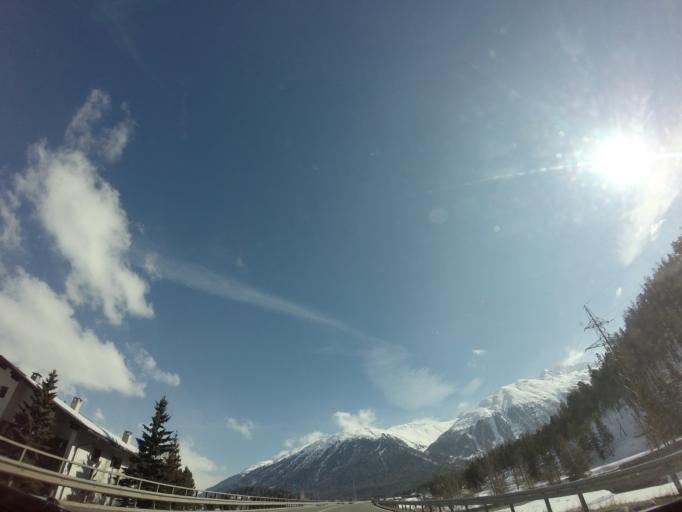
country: CH
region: Grisons
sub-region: Maloja District
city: Celerina
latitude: 46.5092
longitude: 9.8617
